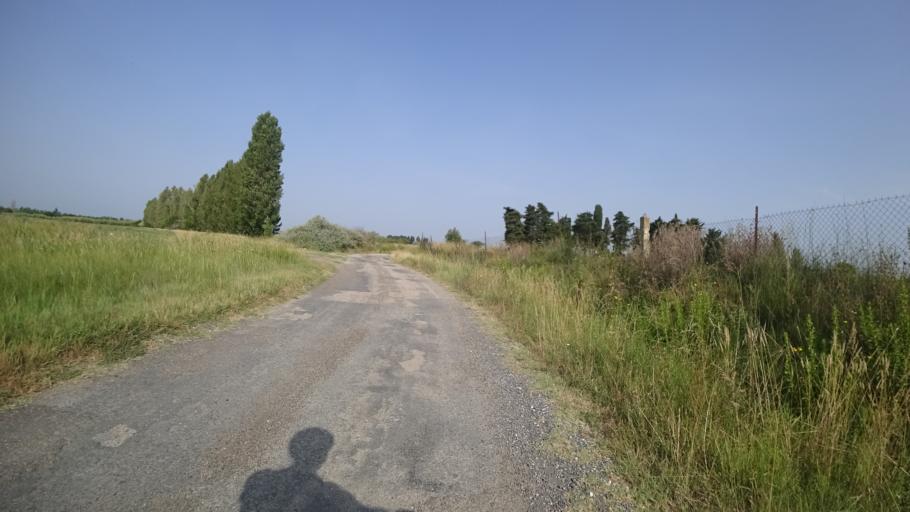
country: FR
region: Languedoc-Roussillon
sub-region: Departement des Pyrenees-Orientales
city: Sainte-Marie-Plage
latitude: 42.7311
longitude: 3.0124
